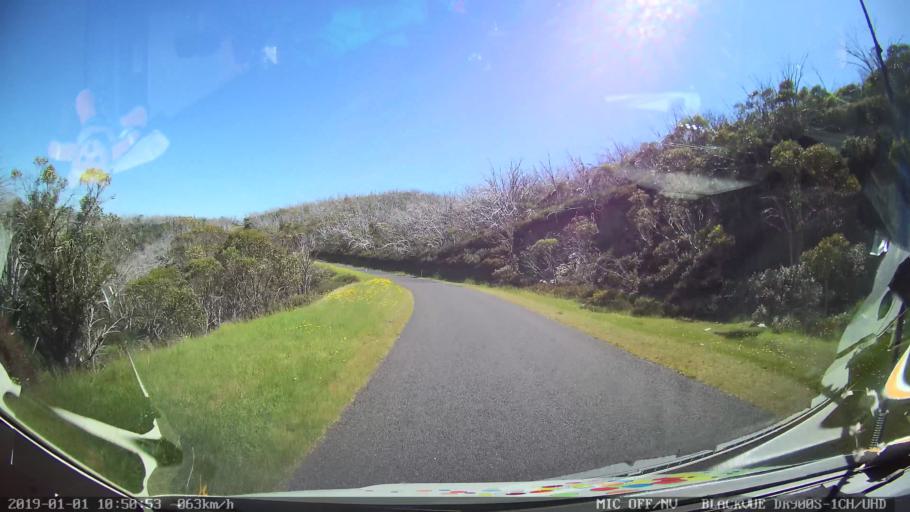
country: AU
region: New South Wales
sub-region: Snowy River
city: Jindabyne
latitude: -36.0241
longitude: 148.3721
